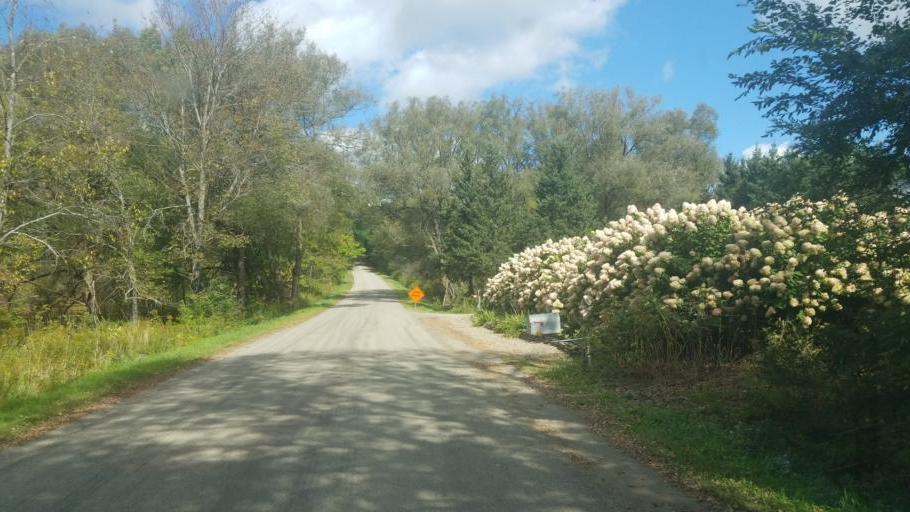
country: US
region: New York
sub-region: Allegany County
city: Cuba
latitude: 42.1941
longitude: -78.3090
